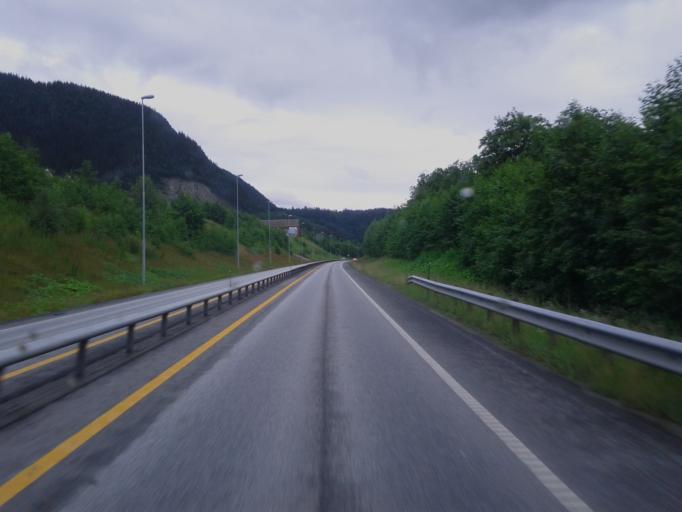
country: NO
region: Sor-Trondelag
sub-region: Melhus
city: Melhus
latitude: 63.2664
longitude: 10.2860
